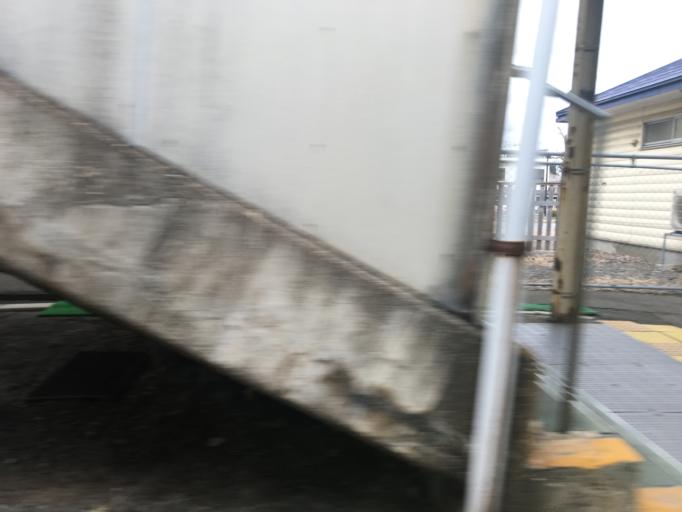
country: JP
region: Aomori
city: Shimokizukuri
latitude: 40.7753
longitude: 140.2205
